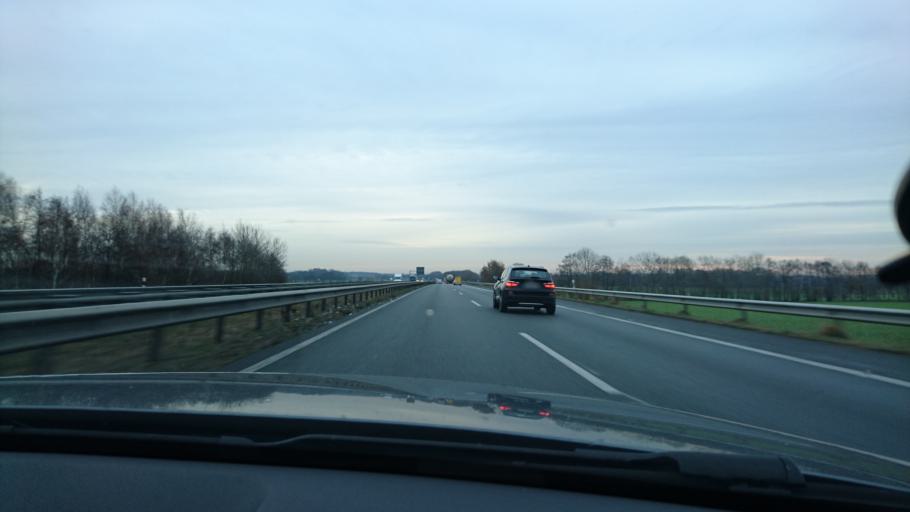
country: DE
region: Lower Saxony
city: Salzbergen
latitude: 52.3386
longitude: 7.2902
